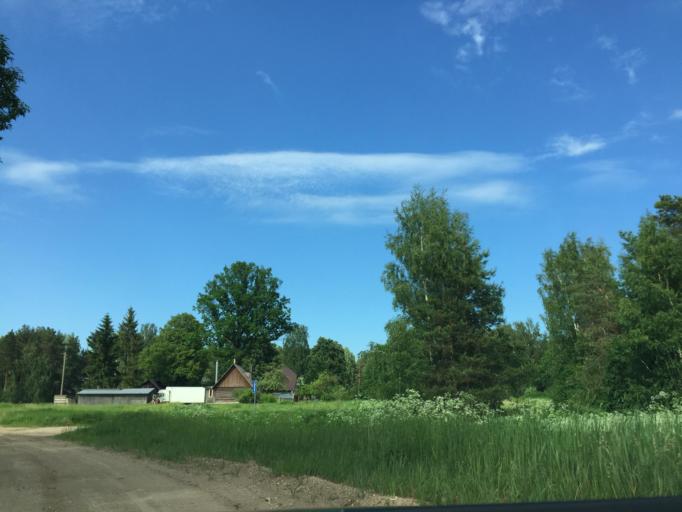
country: LV
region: Stopini
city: Ulbroka
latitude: 56.9263
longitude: 24.2975
